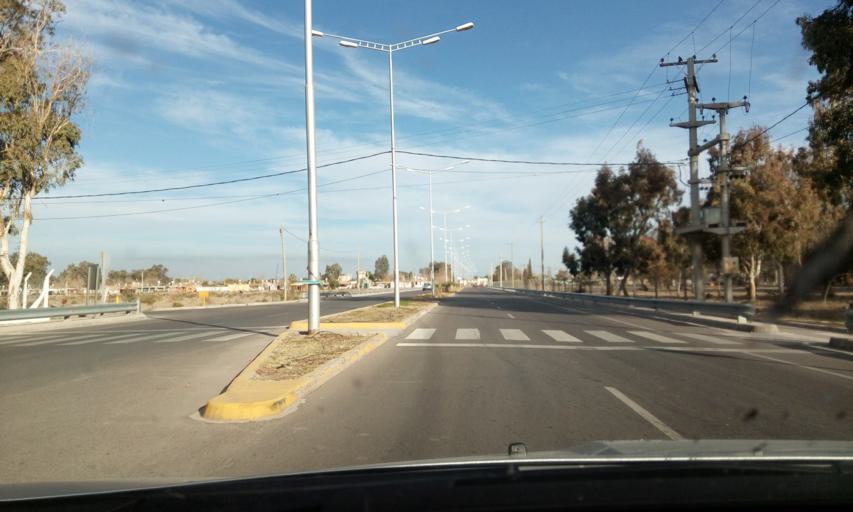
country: AR
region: San Juan
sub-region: Departamento de Rivadavia
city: Rivadavia
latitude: -31.5203
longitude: -68.6291
